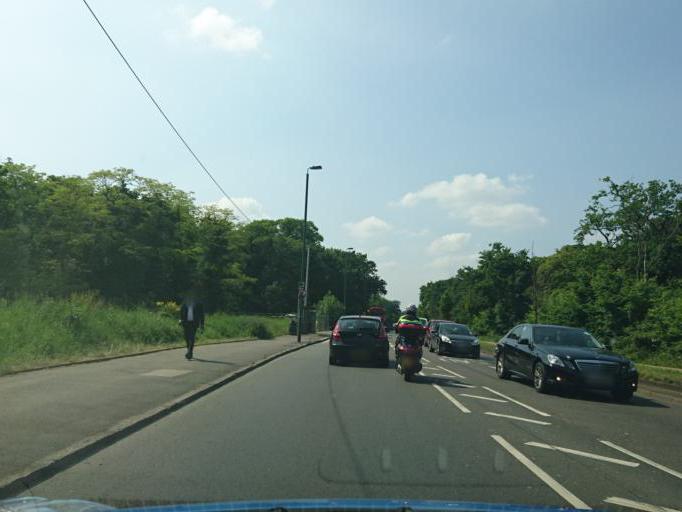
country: GB
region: England
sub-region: Greater London
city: Walthamstow
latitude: 51.5783
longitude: 0.0079
